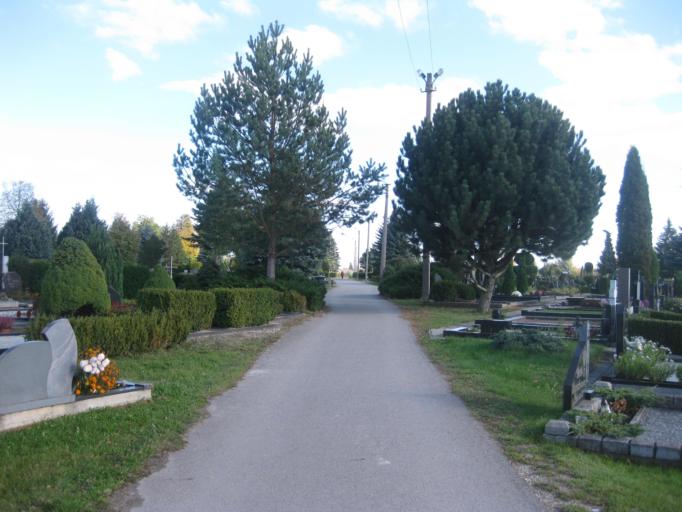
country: LT
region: Kauno apskritis
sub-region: Kauno rajonas
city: Garliava
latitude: 54.8415
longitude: 23.8672
